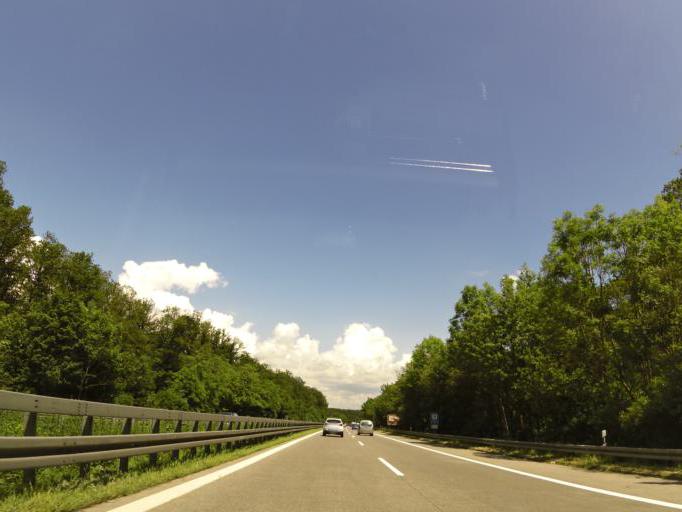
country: DE
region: Baden-Wuerttemberg
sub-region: Tuebingen Region
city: Nerenstetten
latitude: 48.5284
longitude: 10.0853
